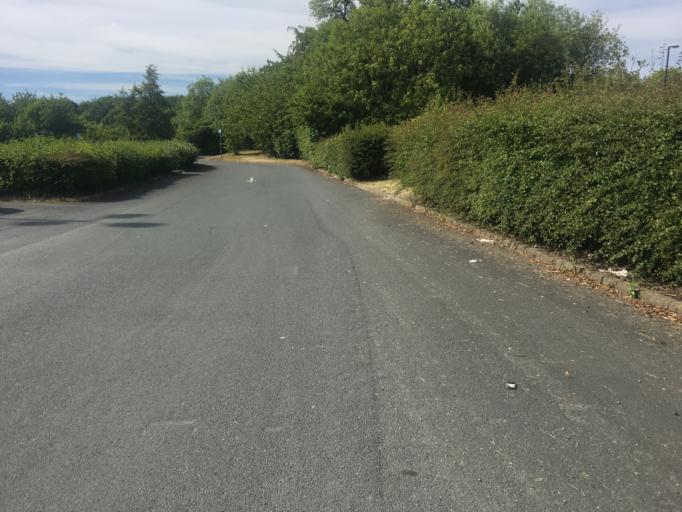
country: GB
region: England
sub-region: Sunderland
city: Washington
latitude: 54.8868
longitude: -1.5397
